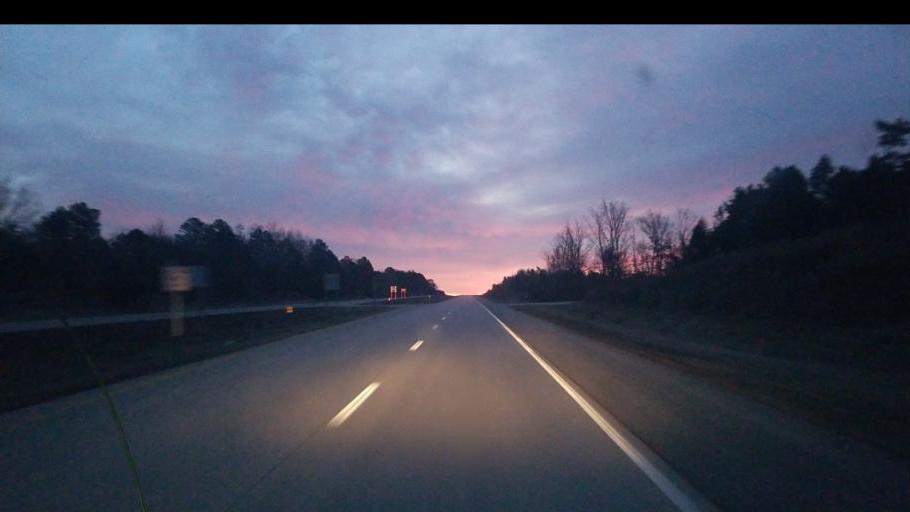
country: US
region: Missouri
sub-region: Shannon County
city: Winona
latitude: 36.9985
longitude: -91.4111
